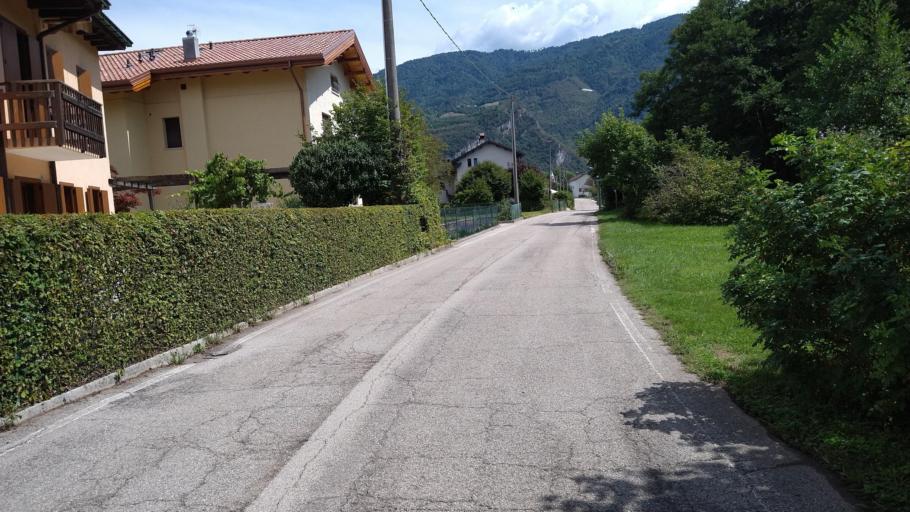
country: IT
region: Veneto
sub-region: Provincia di Belluno
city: Villabruna-Umin
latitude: 46.0116
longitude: 11.9621
